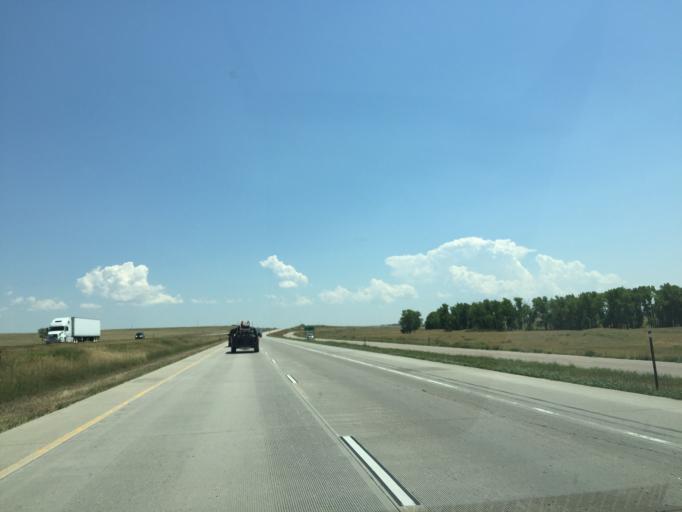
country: US
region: Colorado
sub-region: Arapahoe County
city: Byers
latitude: 39.4941
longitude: -103.9622
